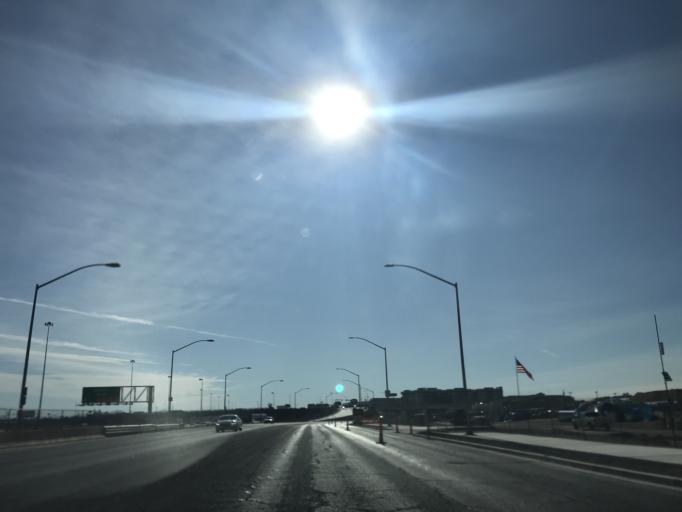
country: US
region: Nevada
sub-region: Clark County
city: Paradise
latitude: 36.0906
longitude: -115.1814
